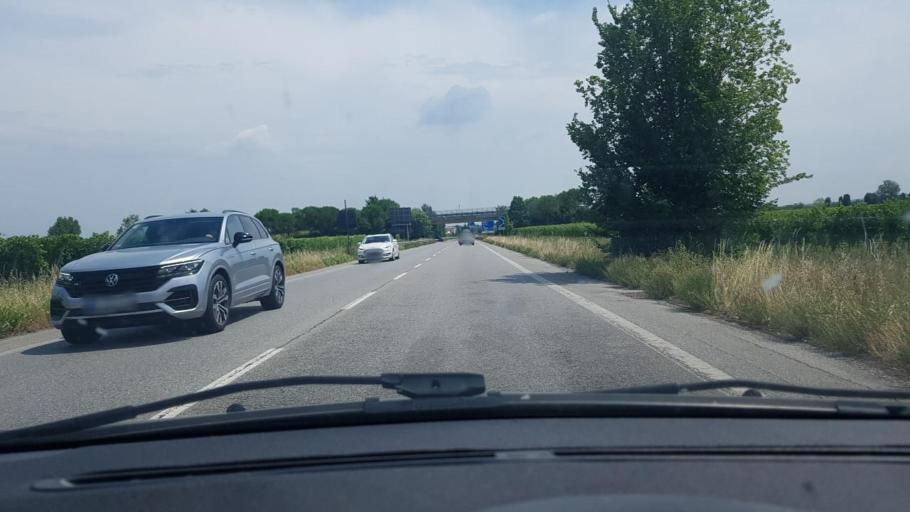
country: IT
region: Lombardy
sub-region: Provincia di Brescia
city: San Martino della Battaglia
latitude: 45.4449
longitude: 10.6049
